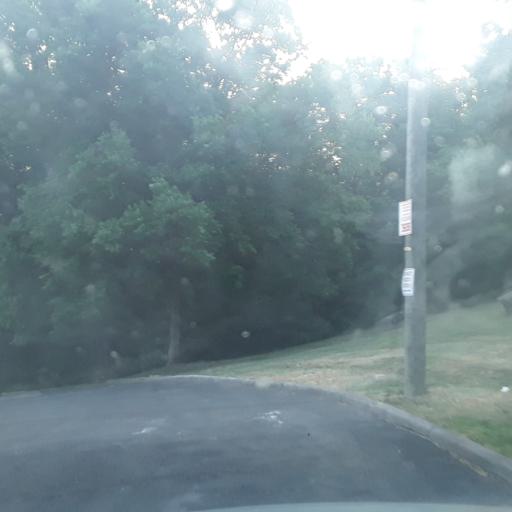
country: US
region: Tennessee
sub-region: Williamson County
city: Brentwood Estates
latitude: 36.0500
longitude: -86.7228
